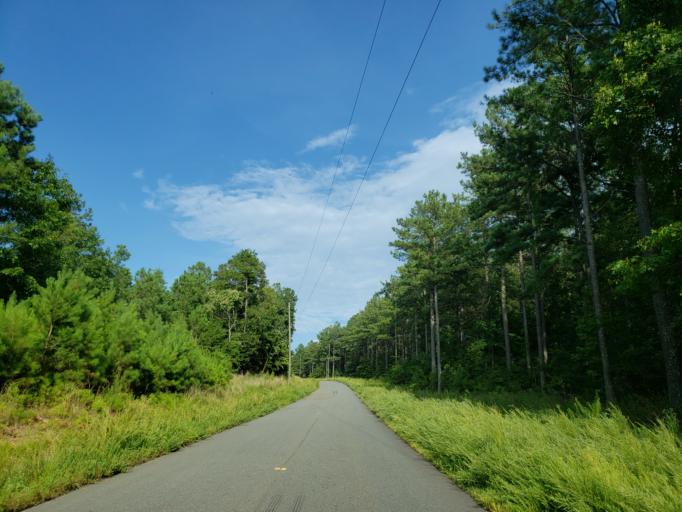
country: US
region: Georgia
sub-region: Bartow County
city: Emerson
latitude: 34.1906
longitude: -84.6558
